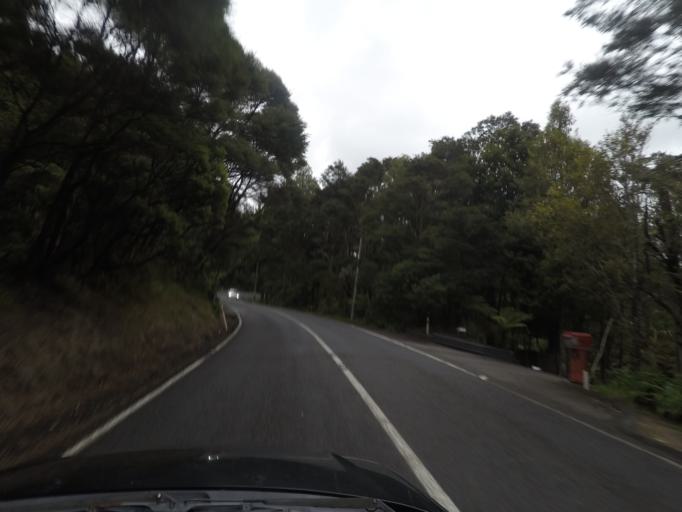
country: NZ
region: Auckland
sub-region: Auckland
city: Titirangi
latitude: -36.9230
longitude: 174.6014
